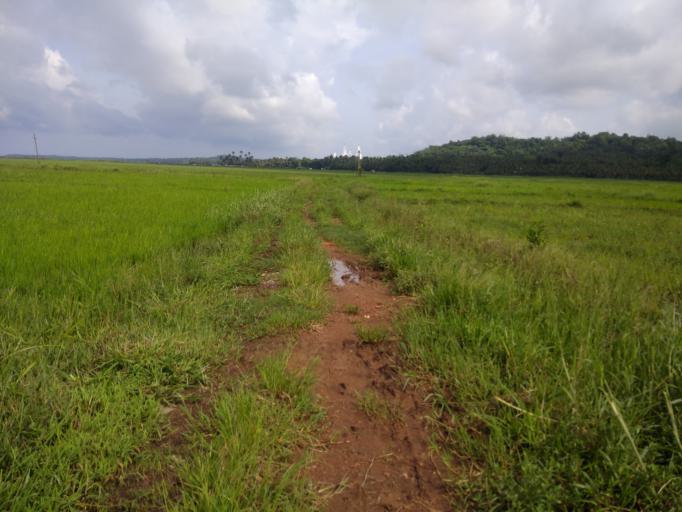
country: IN
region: Kerala
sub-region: Thrissur District
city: Trichur
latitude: 10.5392
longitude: 76.1771
